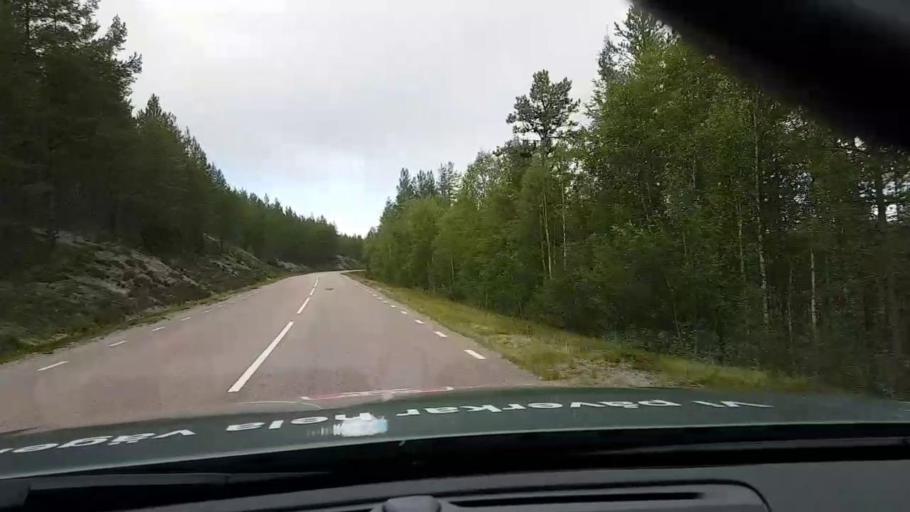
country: SE
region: Vaesterbotten
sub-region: Asele Kommun
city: Asele
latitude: 63.8786
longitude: 17.3561
